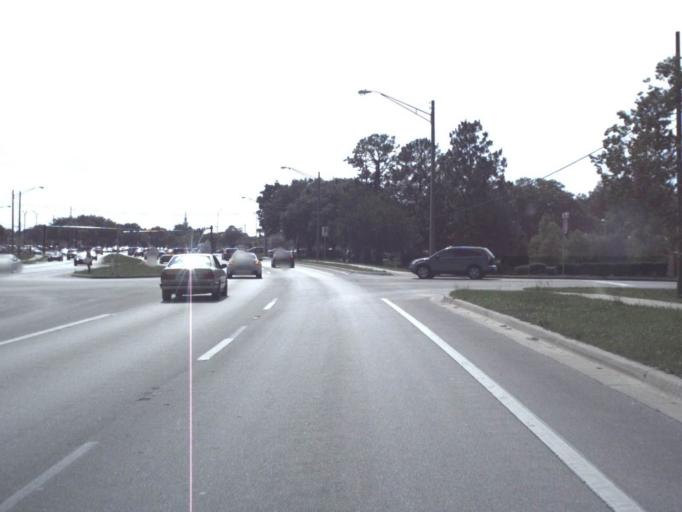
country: US
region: Florida
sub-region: Saint Johns County
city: Fruit Cove
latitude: 30.2184
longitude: -81.5493
